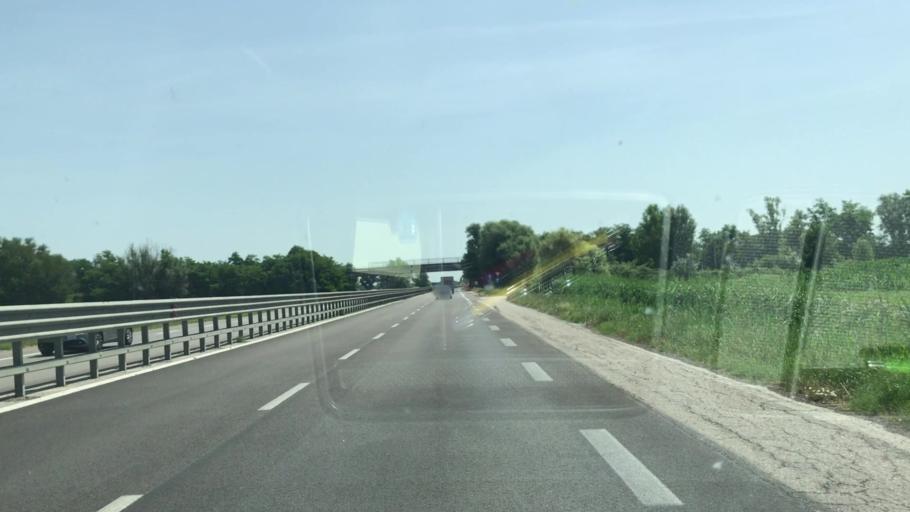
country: IT
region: Veneto
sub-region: Provincia di Rovigo
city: Fratta Polesine
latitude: 45.0234
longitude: 11.6206
